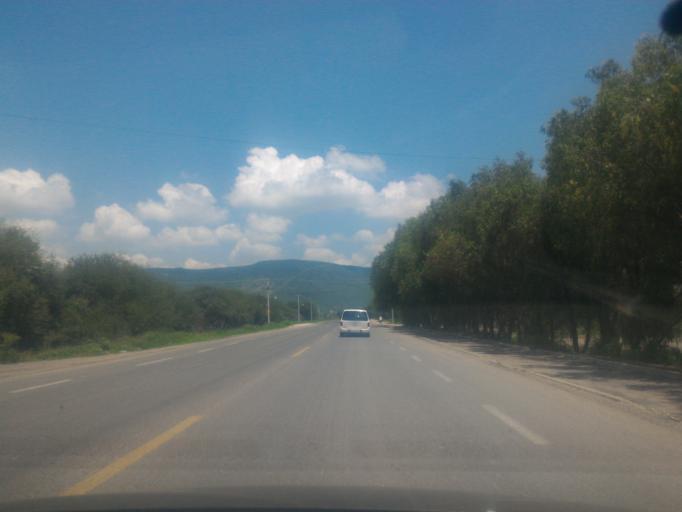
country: MX
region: Guanajuato
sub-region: Purisima del Rincon
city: Monte Grande
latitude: 21.0006
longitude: -101.8650
